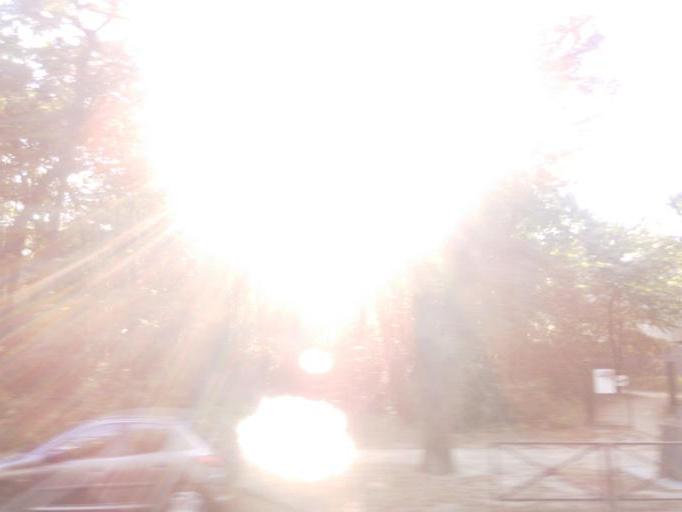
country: FR
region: Ile-de-France
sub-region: Departement des Yvelines
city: Viroflay
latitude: 48.8153
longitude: 2.1507
